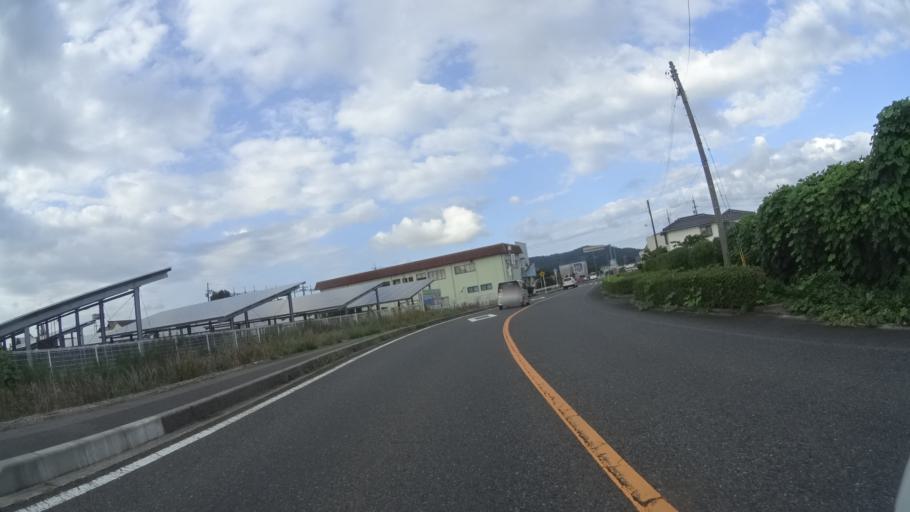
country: JP
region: Tottori
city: Kurayoshi
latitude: 35.4668
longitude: 133.8945
